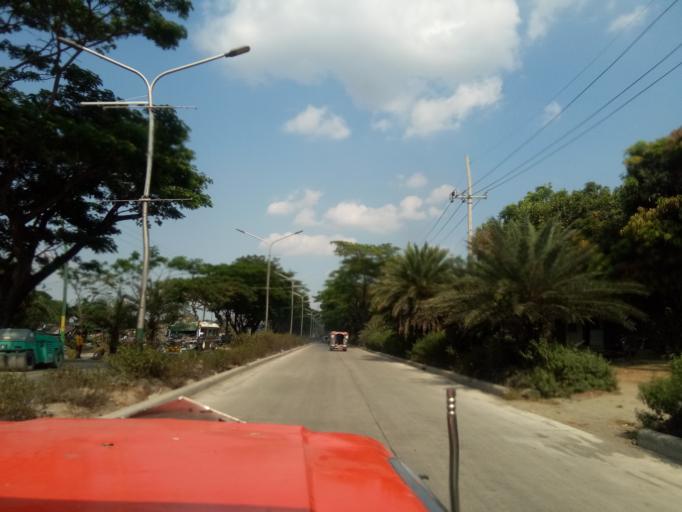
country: PH
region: Calabarzon
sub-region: Province of Cavite
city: Dasmarinas
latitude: 14.3273
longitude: 120.9510
